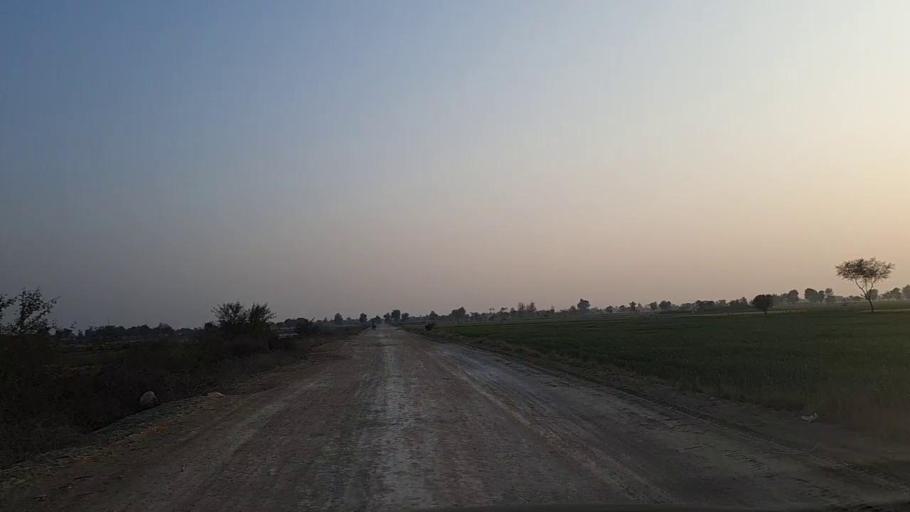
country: PK
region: Sindh
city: Daur
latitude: 26.4237
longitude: 68.3679
